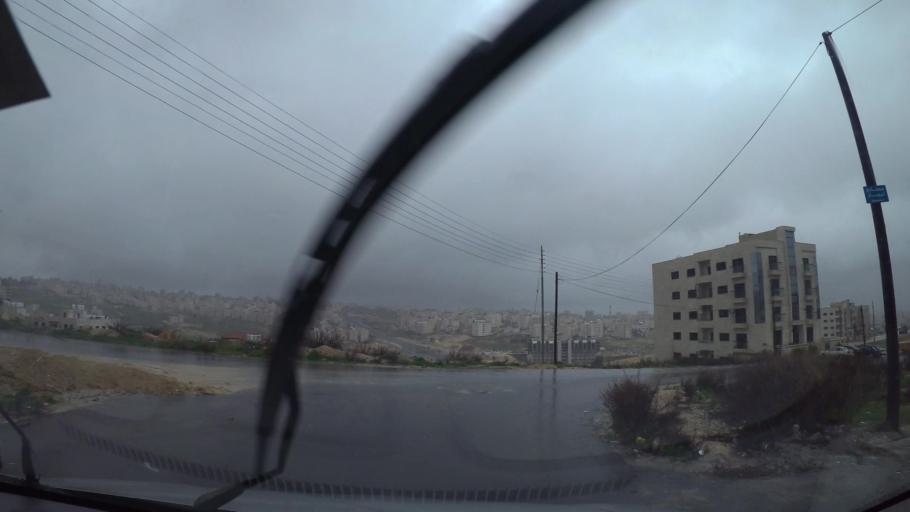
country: JO
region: Amman
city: Al Jubayhah
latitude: 32.0372
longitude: 35.8826
